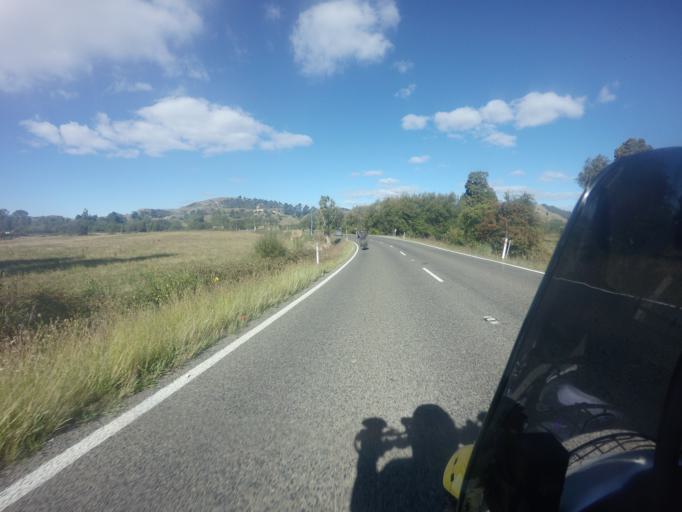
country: NZ
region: Bay of Plenty
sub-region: Opotiki District
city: Opotiki
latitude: -38.0583
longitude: 177.1272
